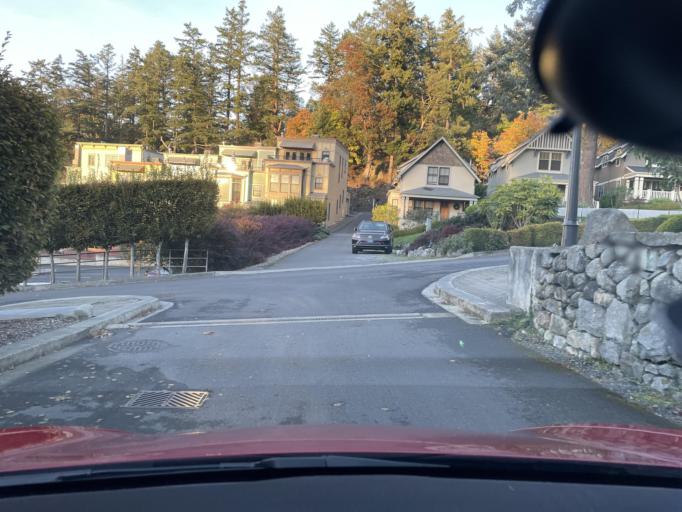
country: US
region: Washington
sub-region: San Juan County
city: Friday Harbor
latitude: 48.6077
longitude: -123.1511
